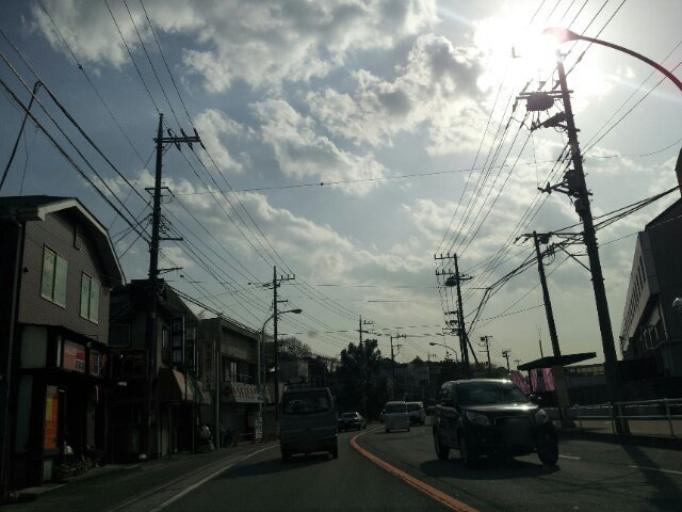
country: JP
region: Kanagawa
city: Yokohama
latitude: 35.4190
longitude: 139.5492
